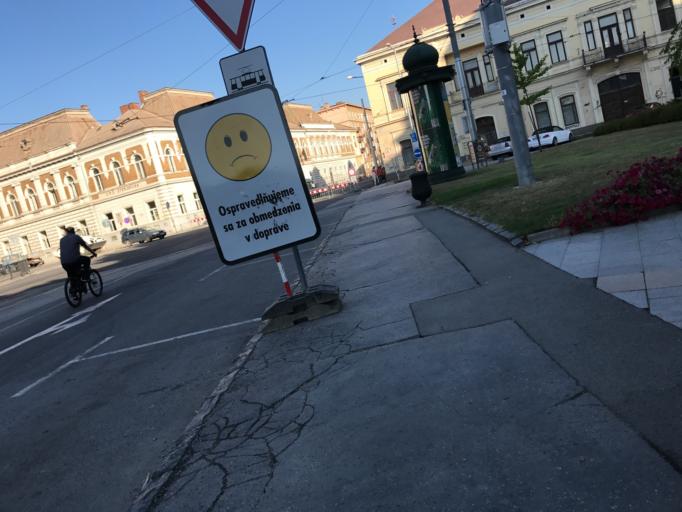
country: SK
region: Kosicky
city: Kosice
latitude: 48.7275
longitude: 21.2542
